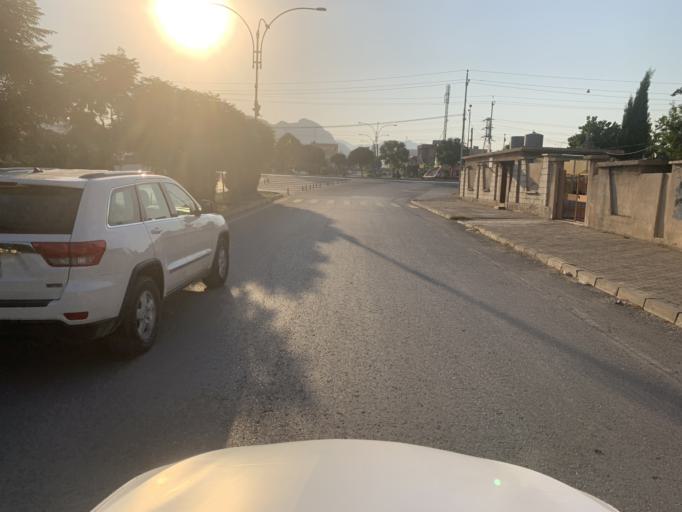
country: IQ
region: As Sulaymaniyah
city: Raniye
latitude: 36.2403
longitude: 44.8762
